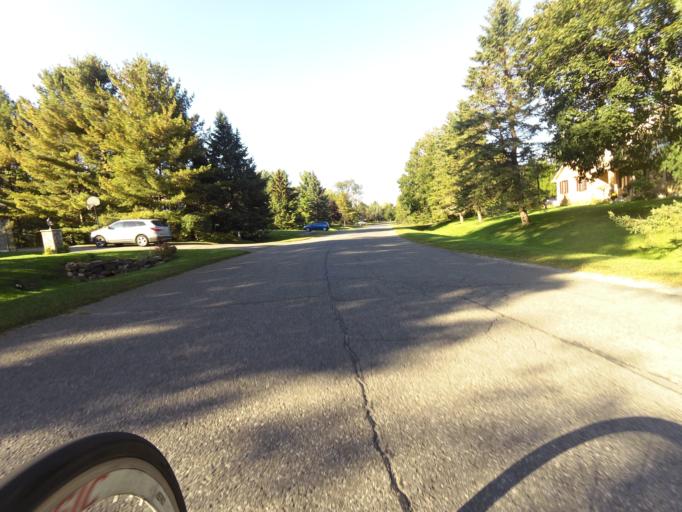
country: CA
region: Ontario
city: Bells Corners
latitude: 45.2236
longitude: -75.6937
